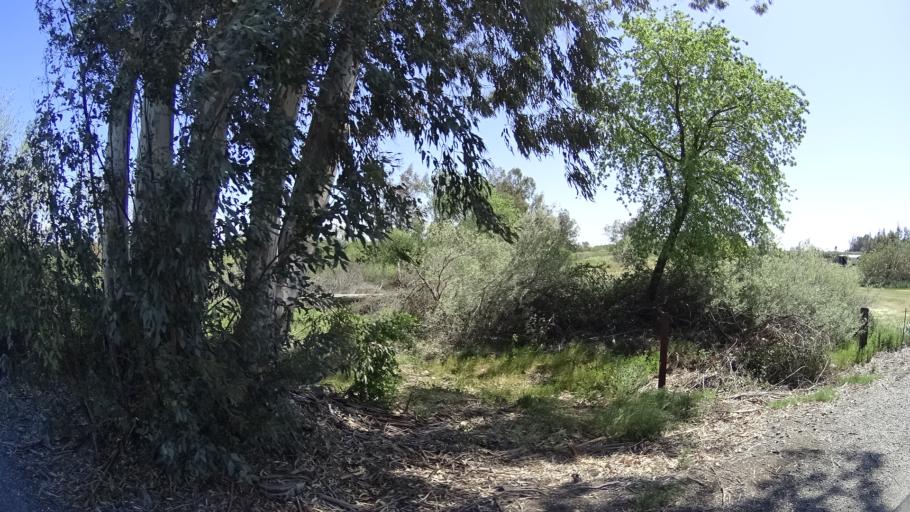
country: US
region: California
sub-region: Glenn County
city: Orland
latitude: 39.7555
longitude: -122.1410
